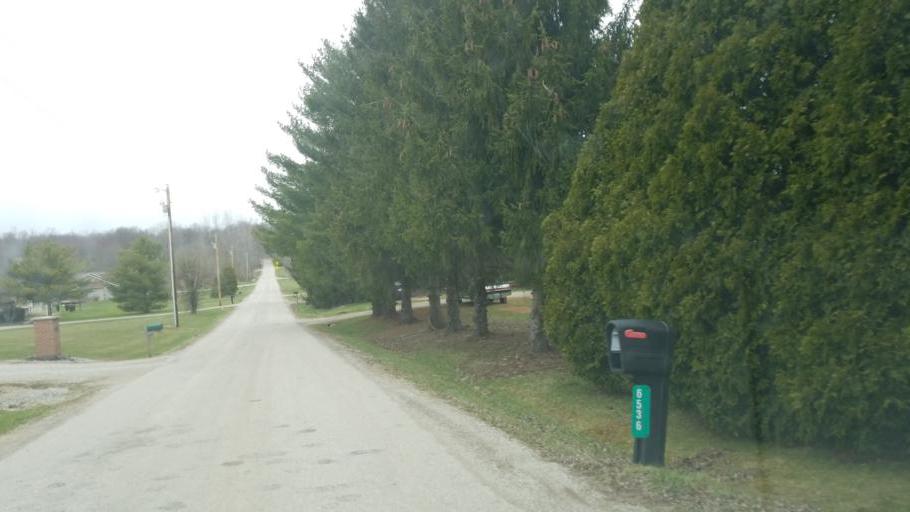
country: US
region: Ohio
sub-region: Knox County
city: Centerburg
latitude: 40.3342
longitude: -82.6474
